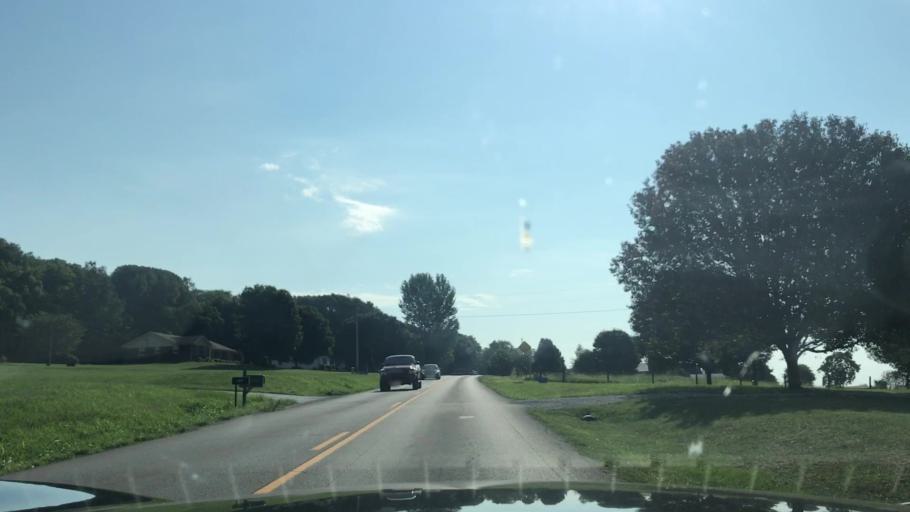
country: US
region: Kentucky
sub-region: Hart County
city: Horse Cave
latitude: 37.1675
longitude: -85.8225
